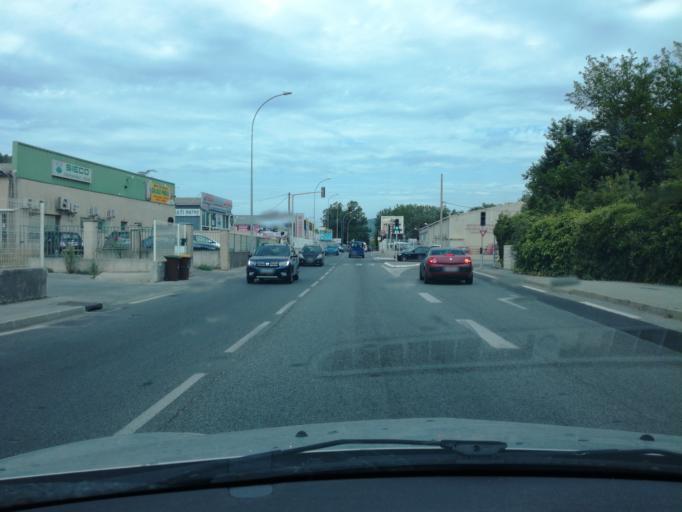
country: FR
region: Provence-Alpes-Cote d'Azur
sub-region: Departement du Var
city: Draguignan
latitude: 43.5223
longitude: 6.4652
